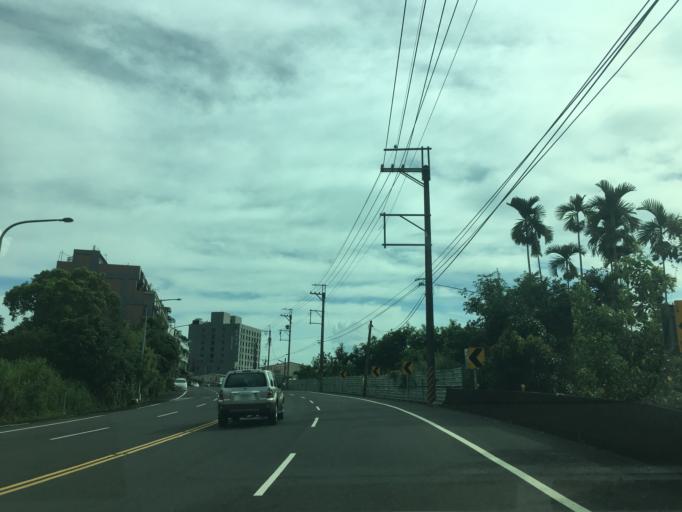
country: TW
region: Taiwan
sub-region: Chiayi
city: Jiayi Shi
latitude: 23.4463
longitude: 120.5459
